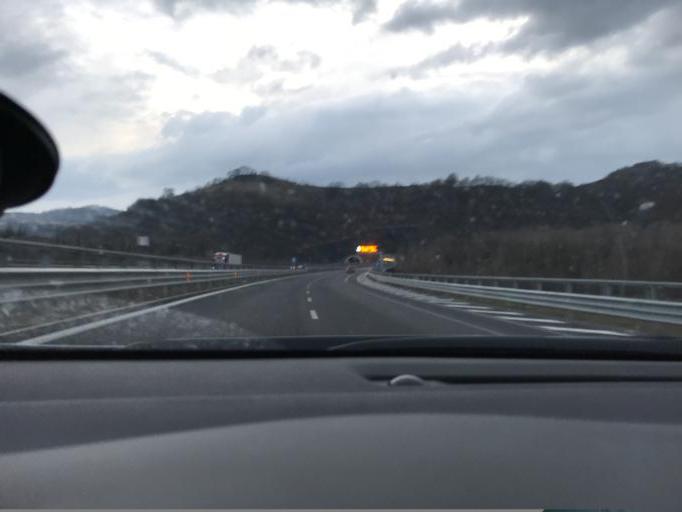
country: IT
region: Umbria
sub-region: Provincia di Perugia
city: Valfabbrica
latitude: 43.1515
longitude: 12.5811
